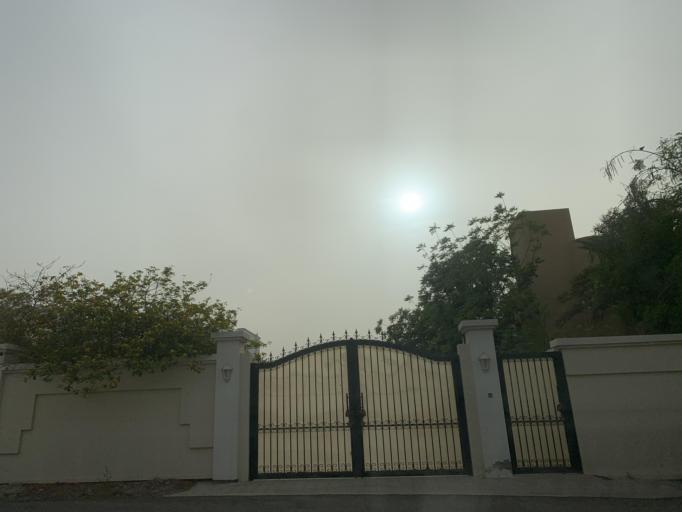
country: BH
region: Northern
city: Ar Rifa'
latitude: 26.1386
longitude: 50.5312
